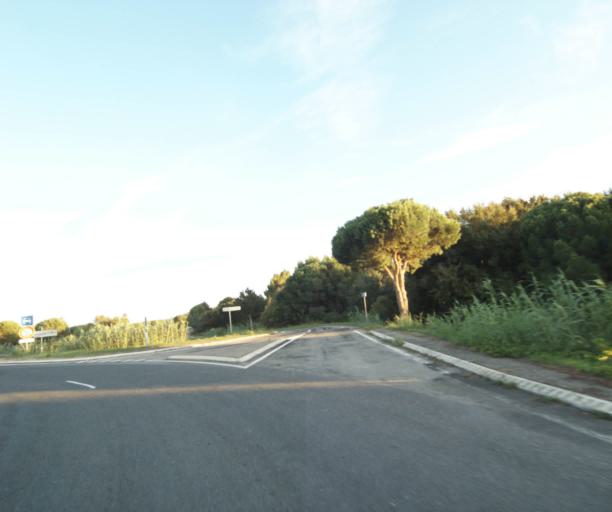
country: FR
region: Languedoc-Roussillon
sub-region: Departement des Pyrenees-Orientales
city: Argelers
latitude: 42.5636
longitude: 3.0037
